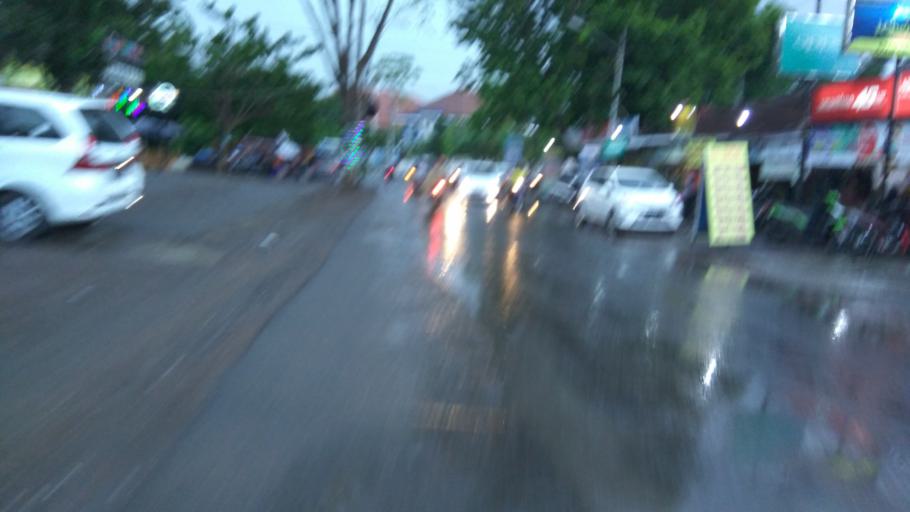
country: ID
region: Central Java
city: Semarang
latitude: -6.9874
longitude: 110.3853
